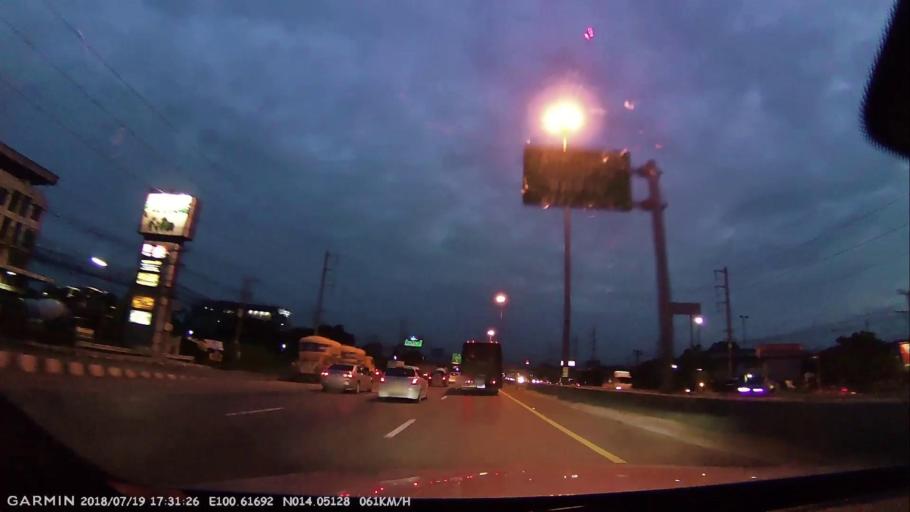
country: TH
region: Pathum Thani
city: Khlong Luang
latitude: 14.0509
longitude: 100.6172
